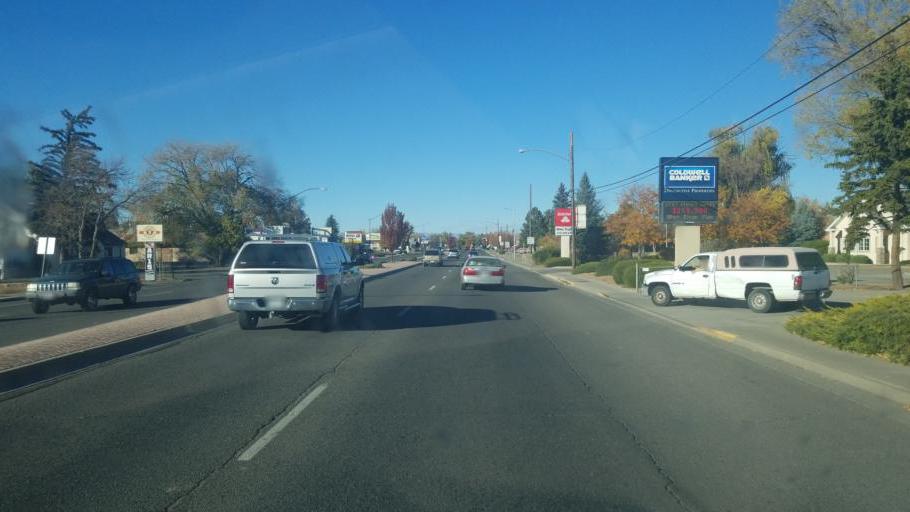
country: US
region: Colorado
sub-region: Montrose County
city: Montrose
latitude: 38.4642
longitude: -107.8662
